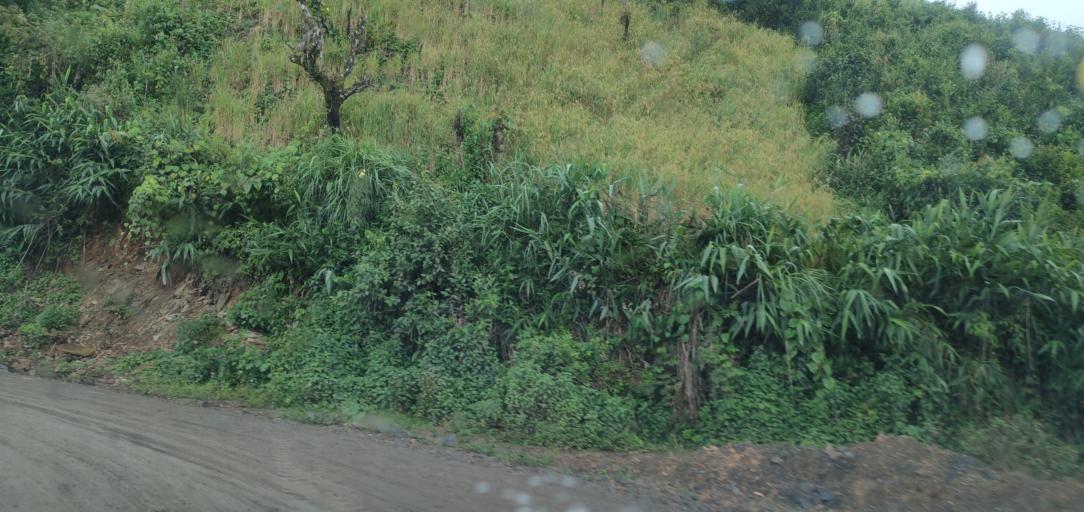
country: LA
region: Phongsali
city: Phongsali
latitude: 21.4299
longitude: 102.1602
